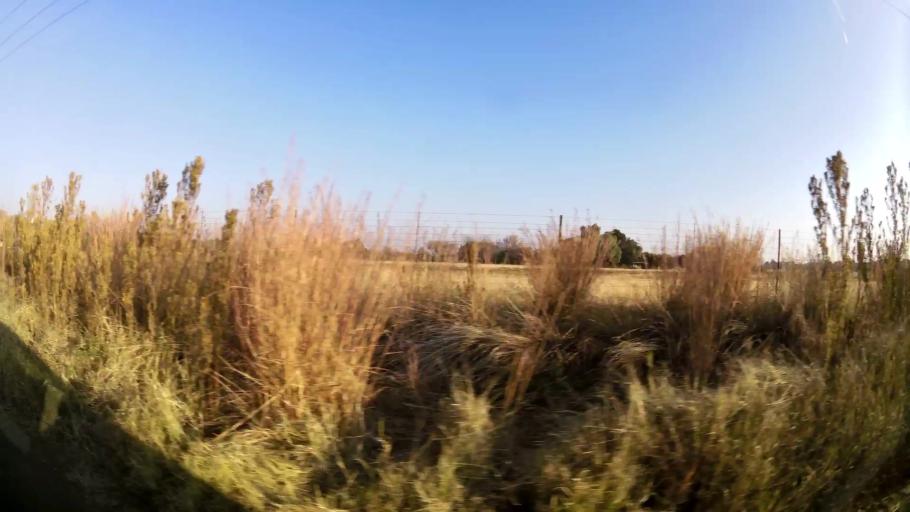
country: ZA
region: Orange Free State
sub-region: Mangaung Metropolitan Municipality
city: Bloemfontein
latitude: -29.0806
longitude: 26.1482
